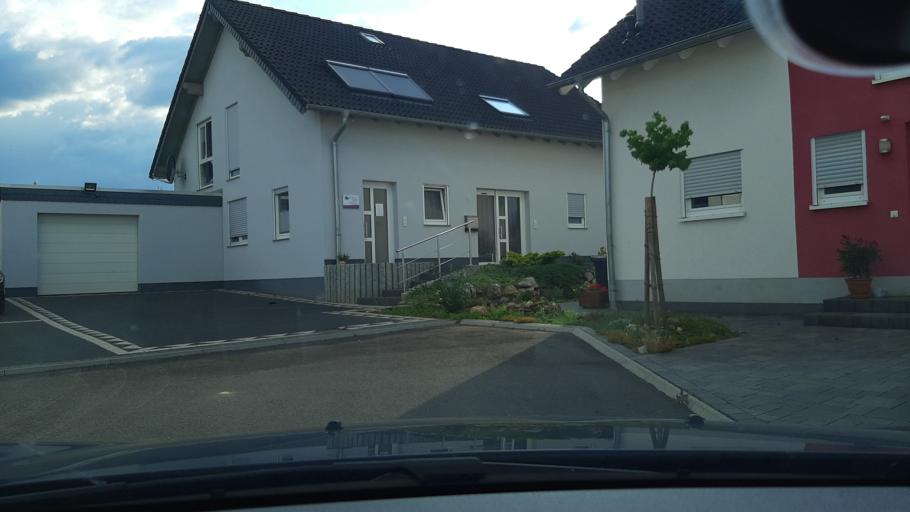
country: DE
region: North Rhine-Westphalia
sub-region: Regierungsbezirk Koln
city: Mechernich
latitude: 50.5897
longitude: 6.6698
